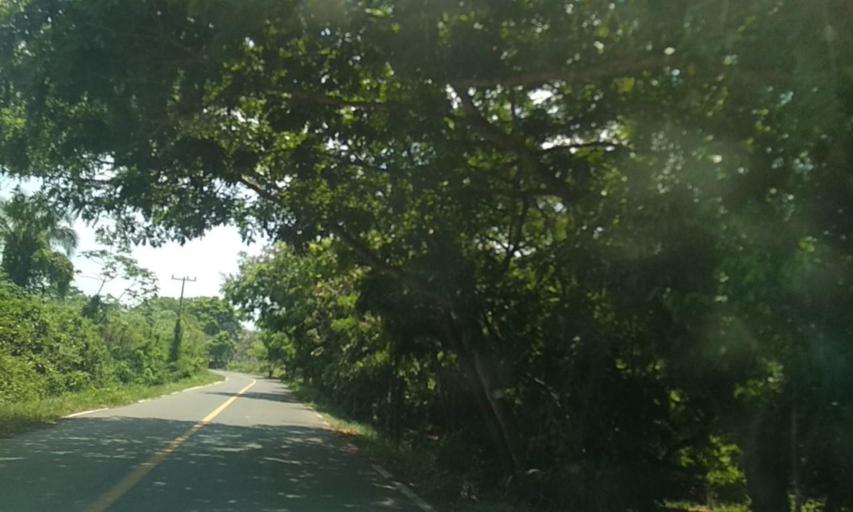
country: MX
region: Tabasco
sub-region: Huimanguillo
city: Francisco Rueda
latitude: 17.7515
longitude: -94.0460
